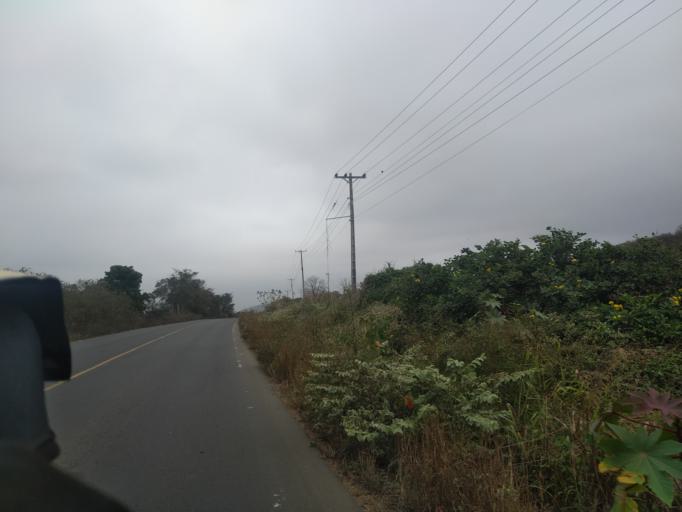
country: EC
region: Manabi
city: Montecristi
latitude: -1.0661
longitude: -80.6578
